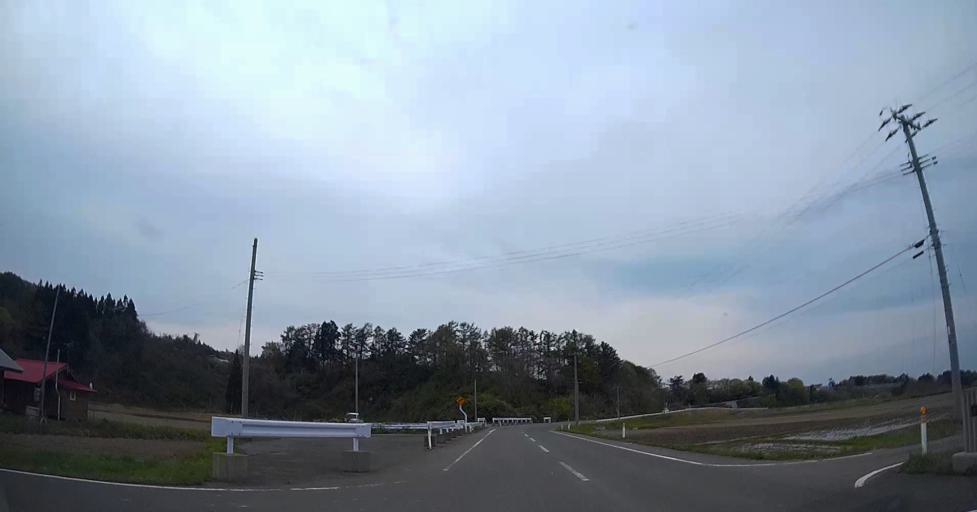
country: JP
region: Aomori
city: Goshogawara
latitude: 40.9011
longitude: 140.4929
